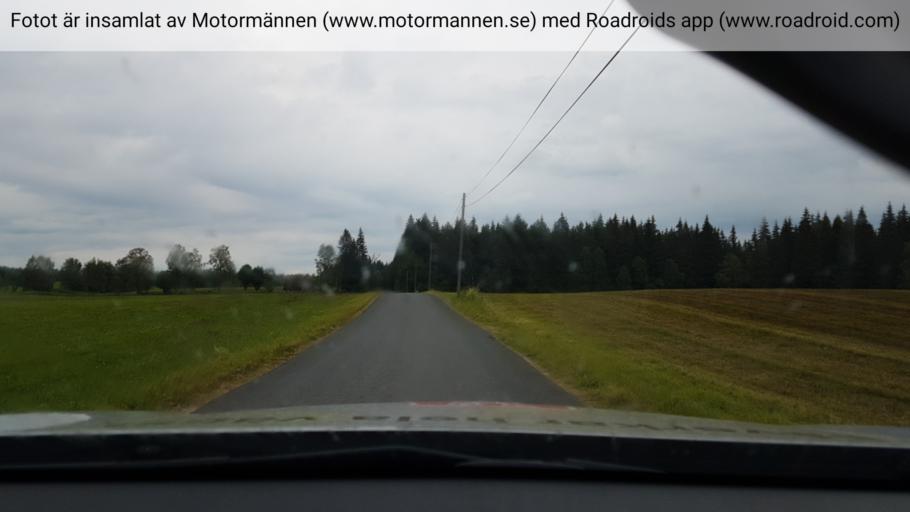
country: SE
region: Joenkoeping
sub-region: Mullsjo Kommun
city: Mullsjoe
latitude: 57.9705
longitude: 13.7460
